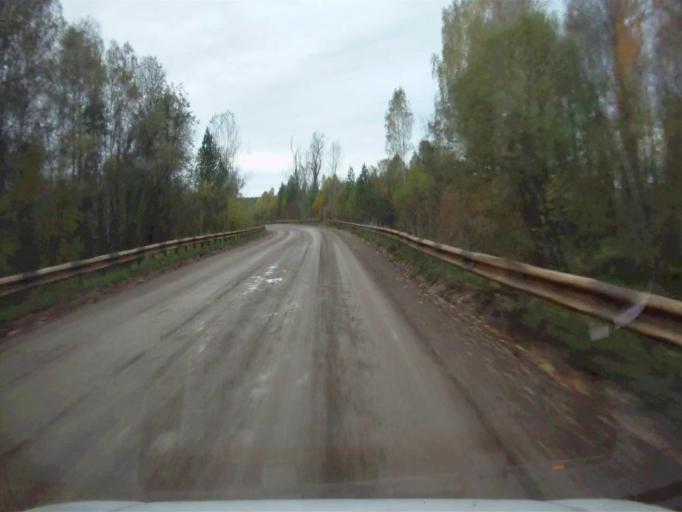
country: RU
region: Chelyabinsk
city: Nyazepetrovsk
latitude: 56.1302
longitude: 59.3267
